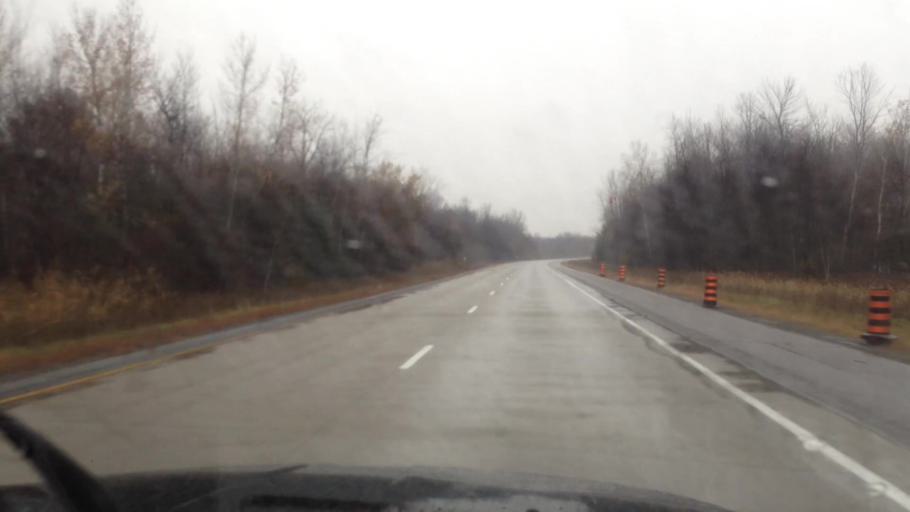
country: CA
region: Ontario
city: Hawkesbury
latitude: 45.4406
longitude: -74.7343
